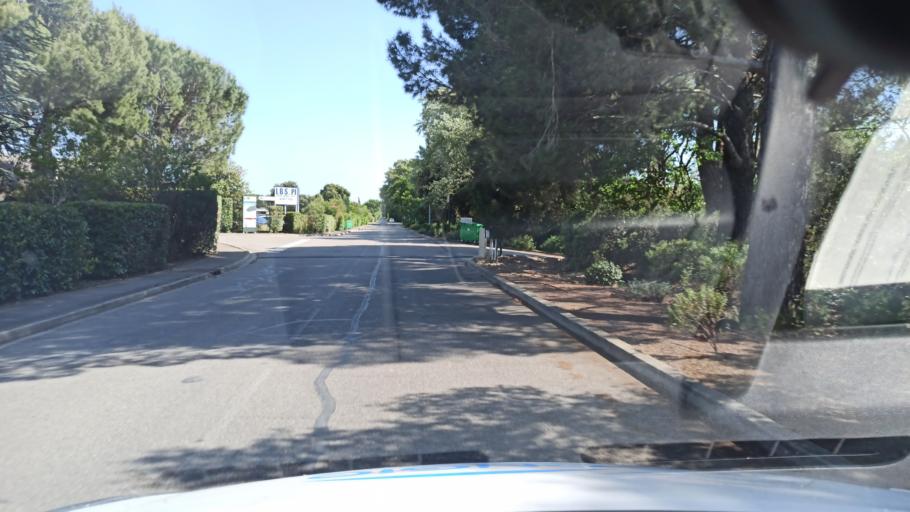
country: FR
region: Provence-Alpes-Cote d'Azur
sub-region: Departement du Vaucluse
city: Vedene
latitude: 43.9608
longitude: 4.8953
